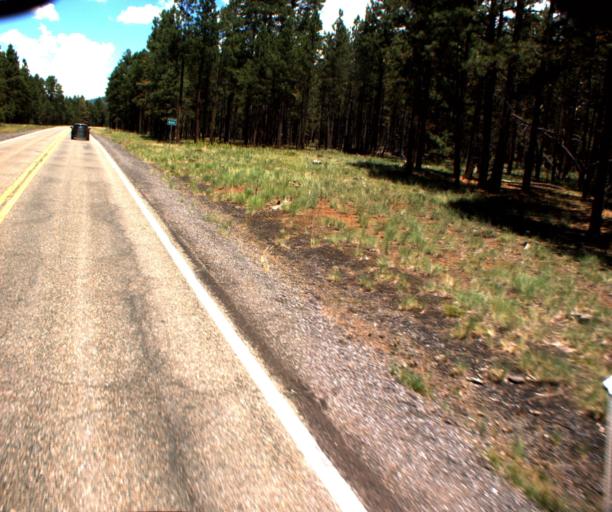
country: US
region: Arizona
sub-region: Coconino County
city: Flagstaff
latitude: 35.3163
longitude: -111.7752
